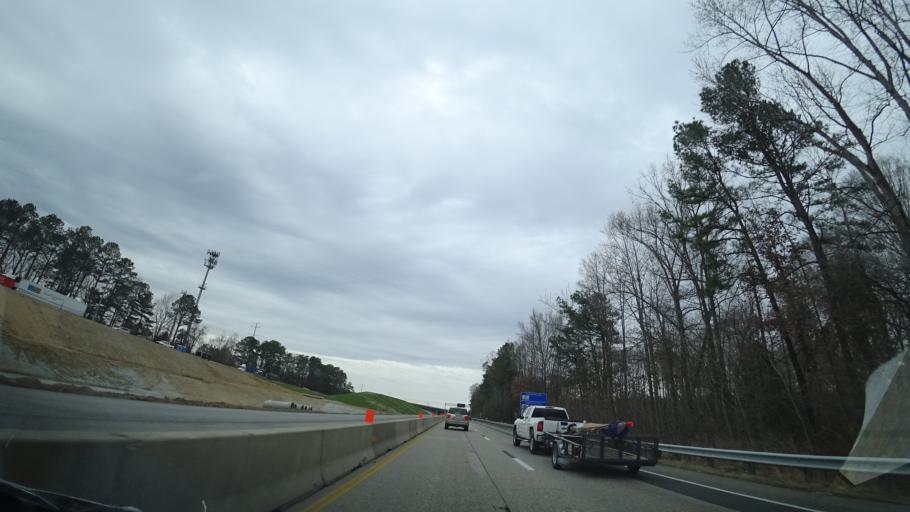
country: US
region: Virginia
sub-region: City of Williamsburg
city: Williamsburg
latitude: 37.2383
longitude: -76.6309
